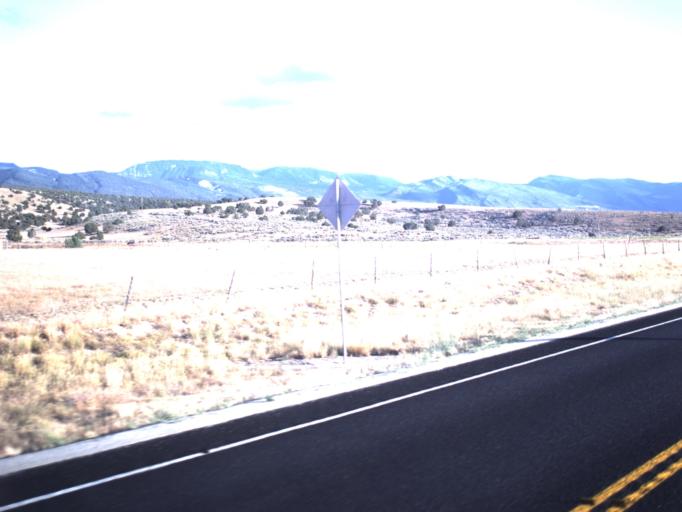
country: US
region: Utah
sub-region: Sanpete County
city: Ephraim
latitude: 39.4252
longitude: -111.5576
